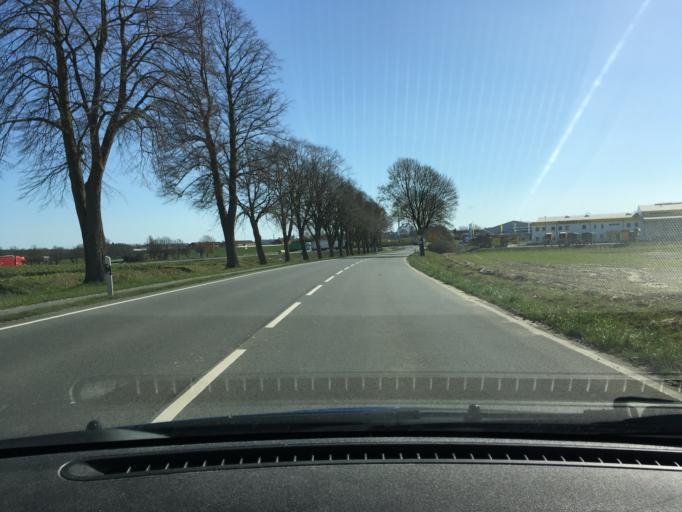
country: DE
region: Lower Saxony
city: Emmendorf
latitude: 52.9983
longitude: 10.5385
